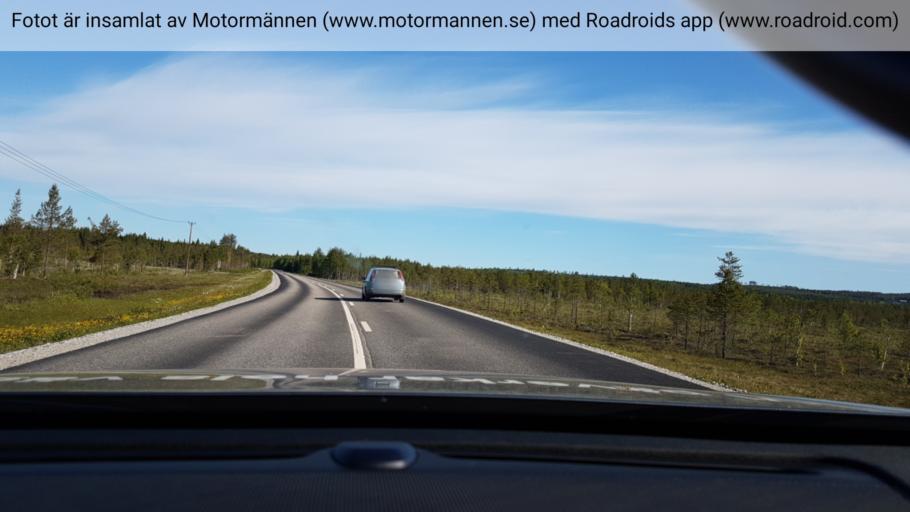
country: SE
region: Vaesterbotten
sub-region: Vannas Kommun
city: Vaennaes
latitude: 64.0392
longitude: 19.6920
